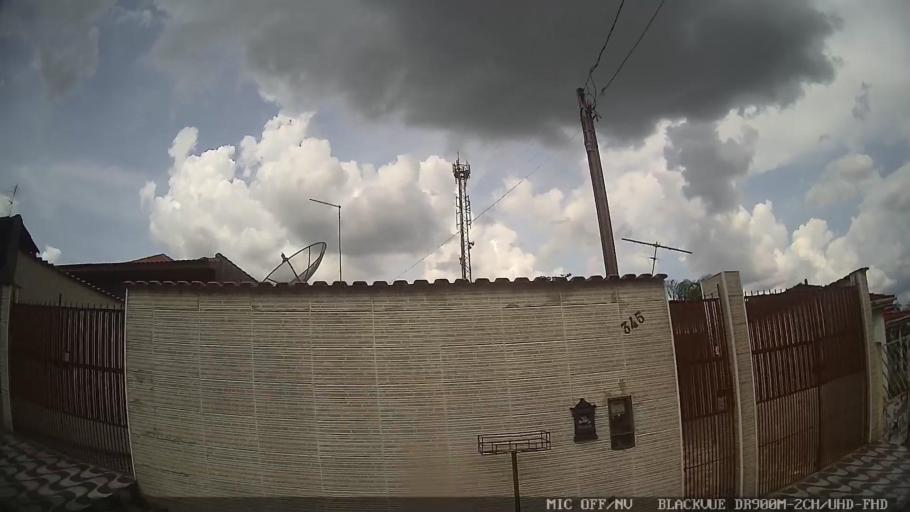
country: BR
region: Sao Paulo
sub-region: Poa
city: Poa
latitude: -23.5258
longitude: -46.3334
